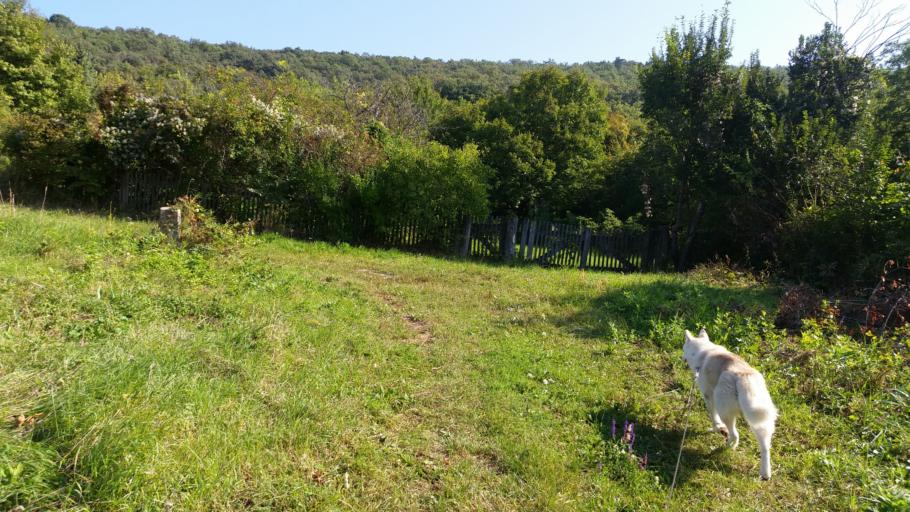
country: HU
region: Pest
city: Telki
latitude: 47.5470
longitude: 18.8394
